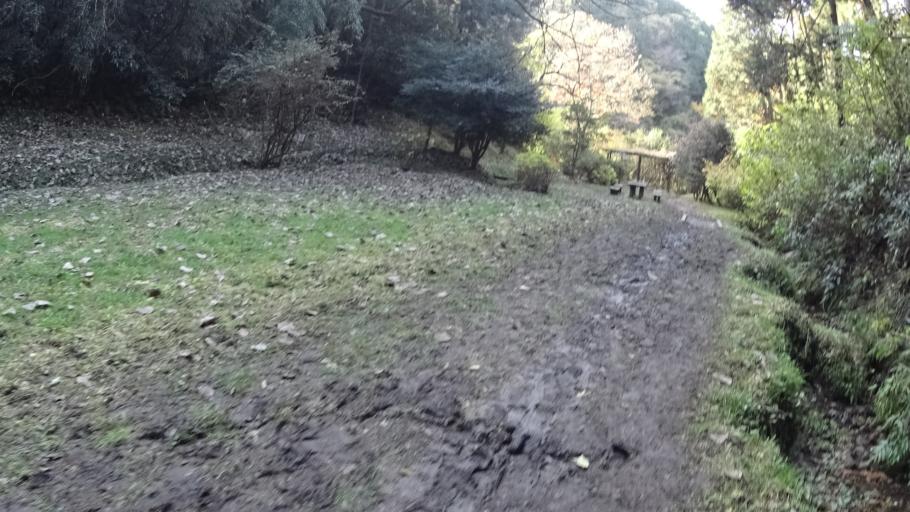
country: JP
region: Kanagawa
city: Kamakura
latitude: 35.3596
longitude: 139.5886
